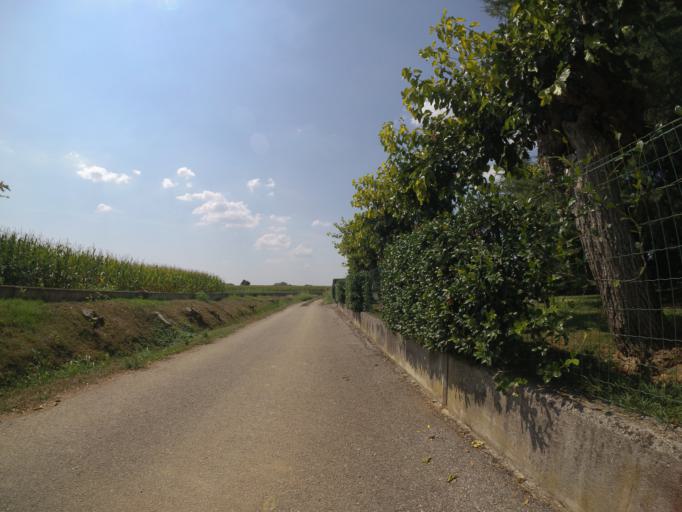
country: IT
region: Friuli Venezia Giulia
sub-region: Provincia di Udine
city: Bertiolo
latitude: 45.9368
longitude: 13.0670
